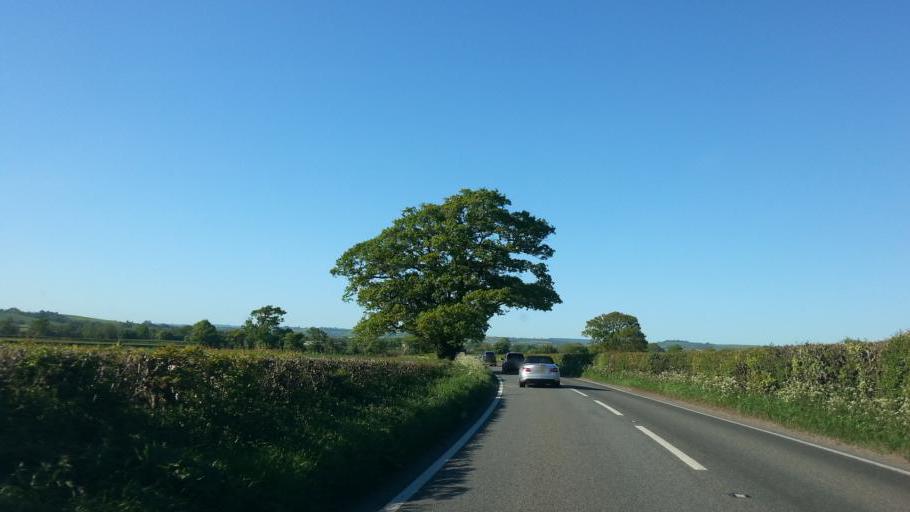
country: GB
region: England
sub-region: Somerset
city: Castle Cary
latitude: 51.1091
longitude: -2.5205
